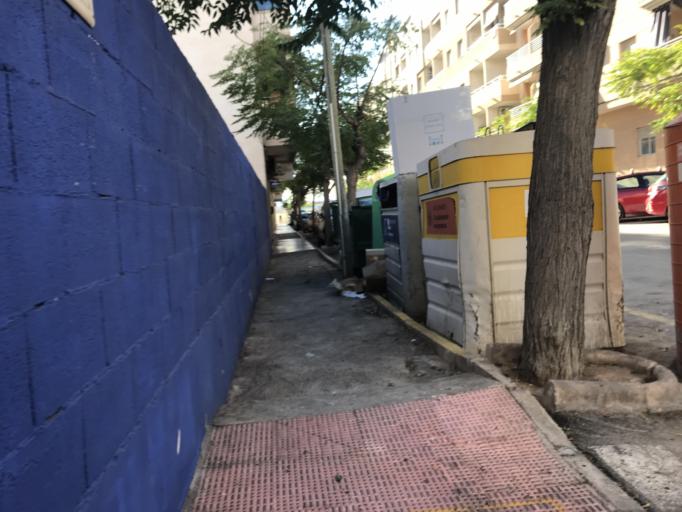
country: ES
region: Valencia
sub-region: Provincia de Alicante
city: Torrevieja
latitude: 37.9800
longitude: -0.6896
